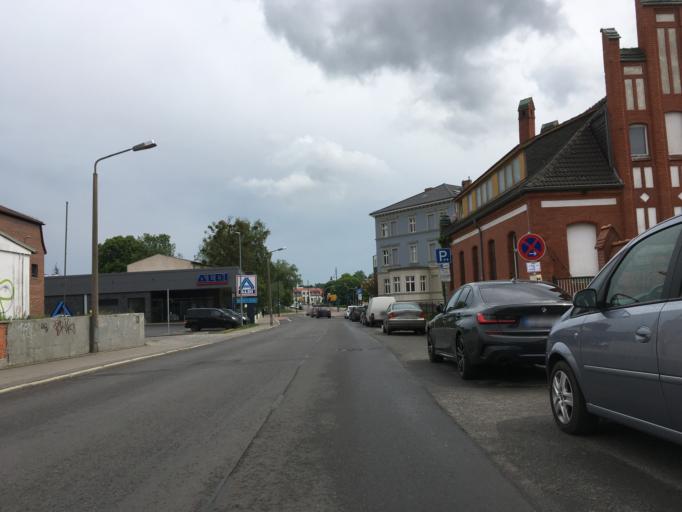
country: DE
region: Brandenburg
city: Eberswalde
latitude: 52.8353
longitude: 13.8144
